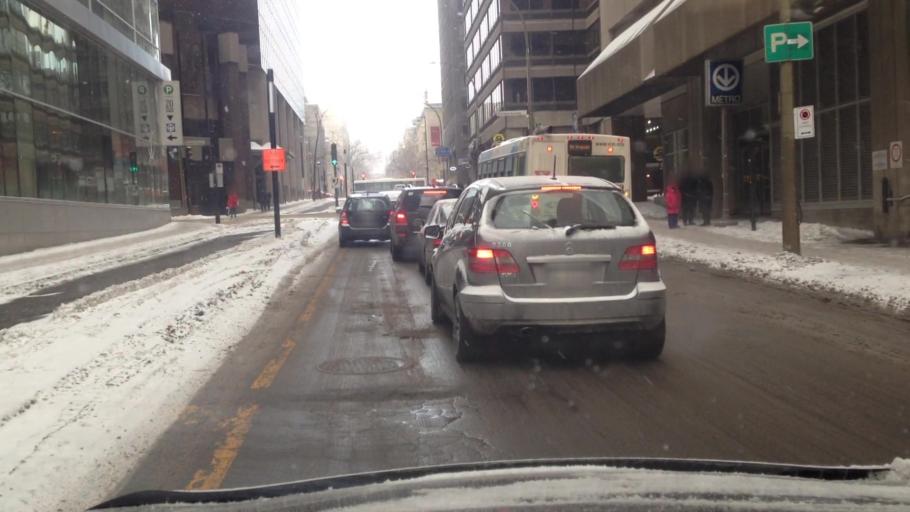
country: CA
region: Quebec
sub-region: Montreal
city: Montreal
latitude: 45.5044
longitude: -73.5720
